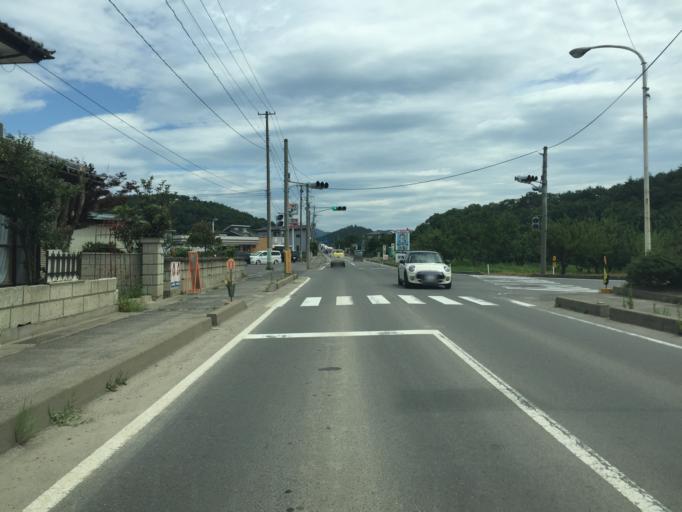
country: JP
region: Fukushima
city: Fukushima-shi
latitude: 37.8081
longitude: 140.4141
